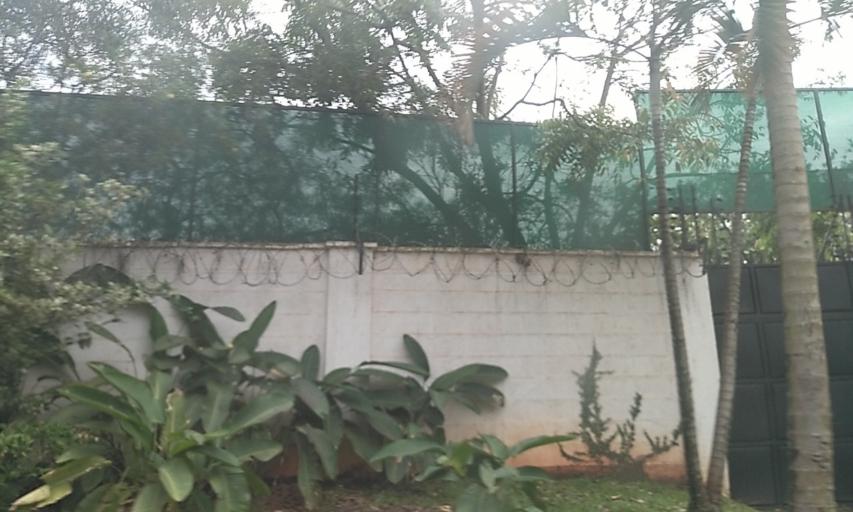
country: UG
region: Central Region
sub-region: Kampala District
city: Kampala
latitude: 0.3321
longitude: 32.5956
